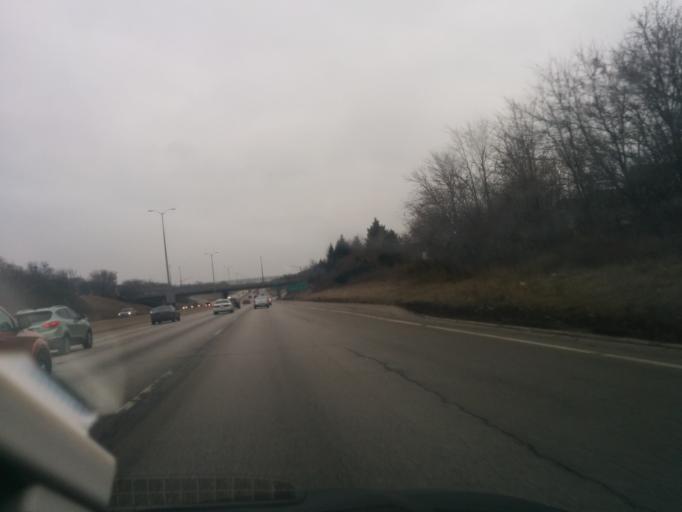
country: US
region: Wisconsin
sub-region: Milwaukee County
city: Shorewood
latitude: 43.0767
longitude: -87.9211
